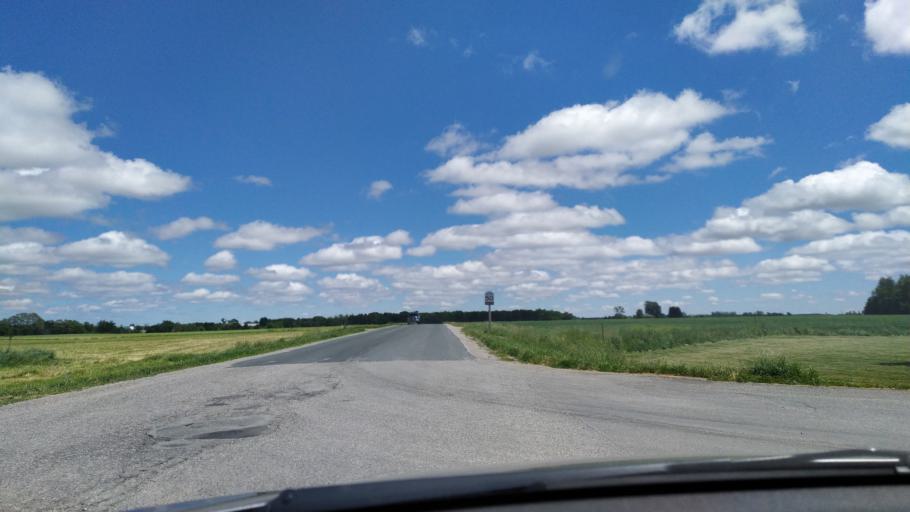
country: CA
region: Ontario
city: Huron East
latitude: 43.4548
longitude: -81.1920
